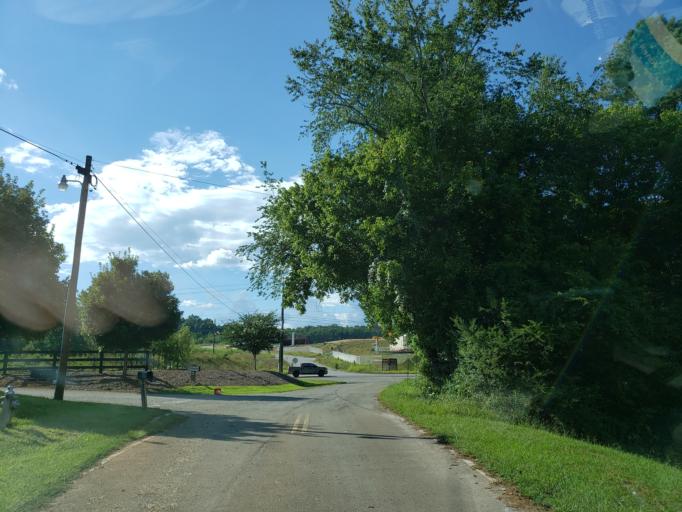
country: US
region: Georgia
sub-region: Cherokee County
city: Canton
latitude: 34.2811
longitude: -84.4407
